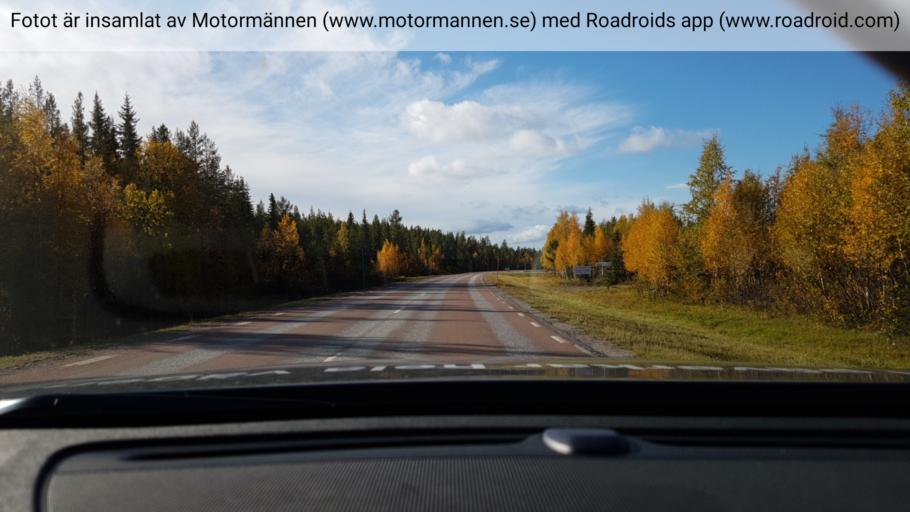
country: SE
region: Norrbotten
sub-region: Arjeplogs Kommun
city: Arjeplog
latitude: 66.0549
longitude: 17.9269
